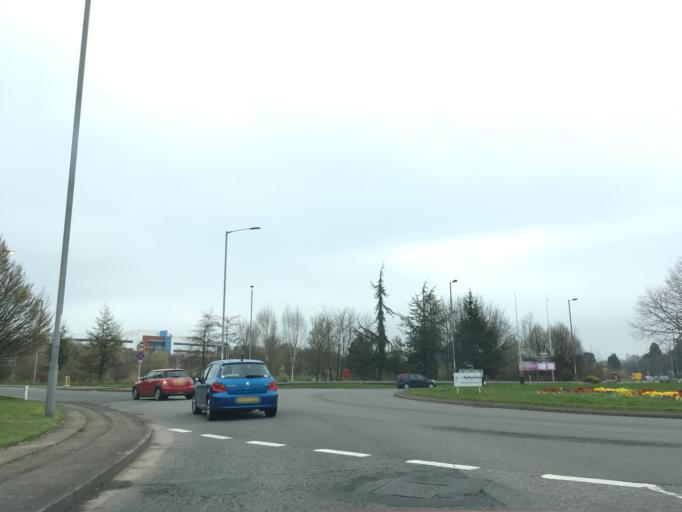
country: GB
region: Wales
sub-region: Newport
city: Marshfield
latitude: 51.5563
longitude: -3.0414
